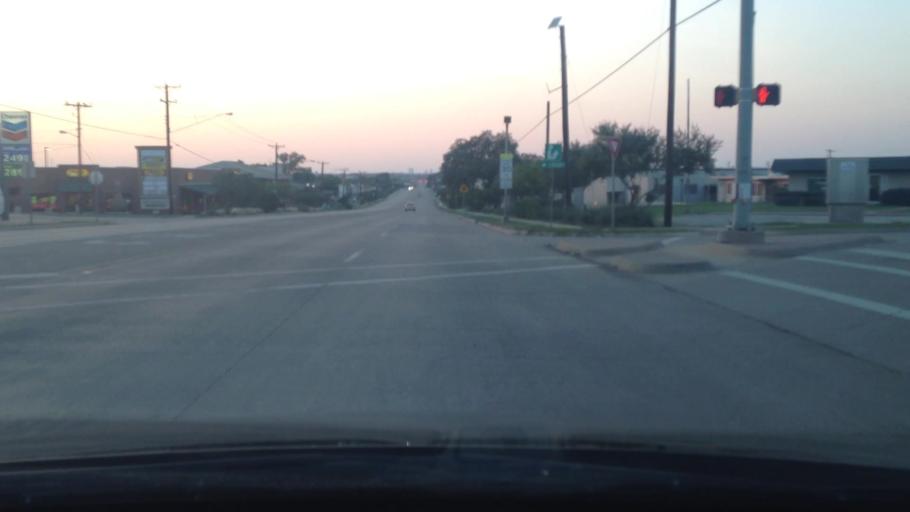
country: US
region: Texas
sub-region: Tarrant County
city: Kennedale
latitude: 32.6467
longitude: -97.2214
